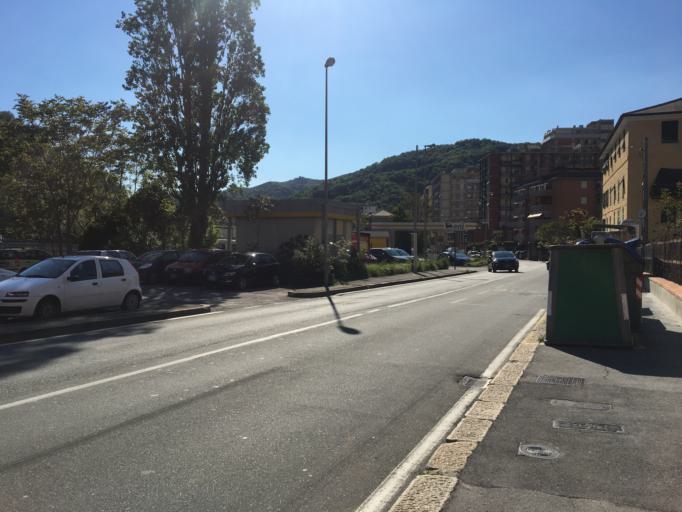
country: IT
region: Liguria
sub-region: Provincia di Genova
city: Piccarello
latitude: 44.4546
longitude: 8.9860
